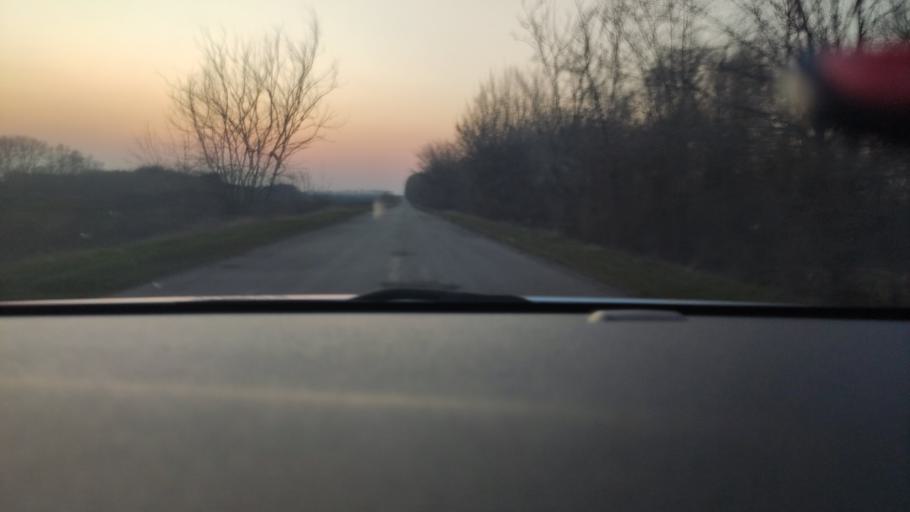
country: RU
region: Voronezj
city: Uryv-Pokrovka
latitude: 51.1245
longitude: 39.1200
